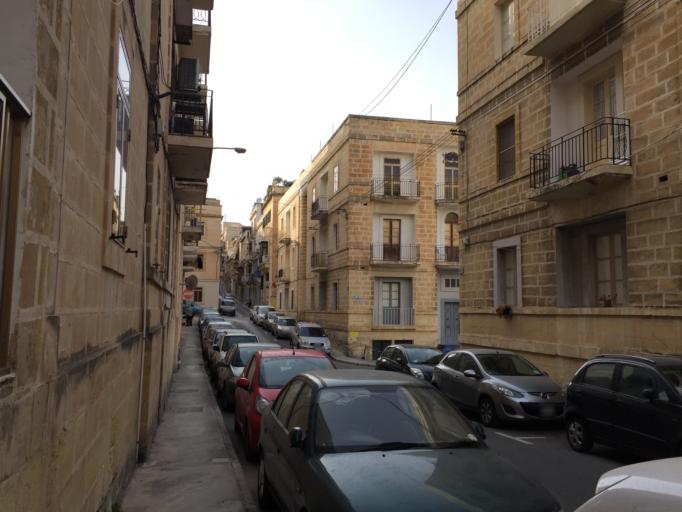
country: MT
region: L-Isla
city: Senglea
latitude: 35.8876
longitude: 14.5174
